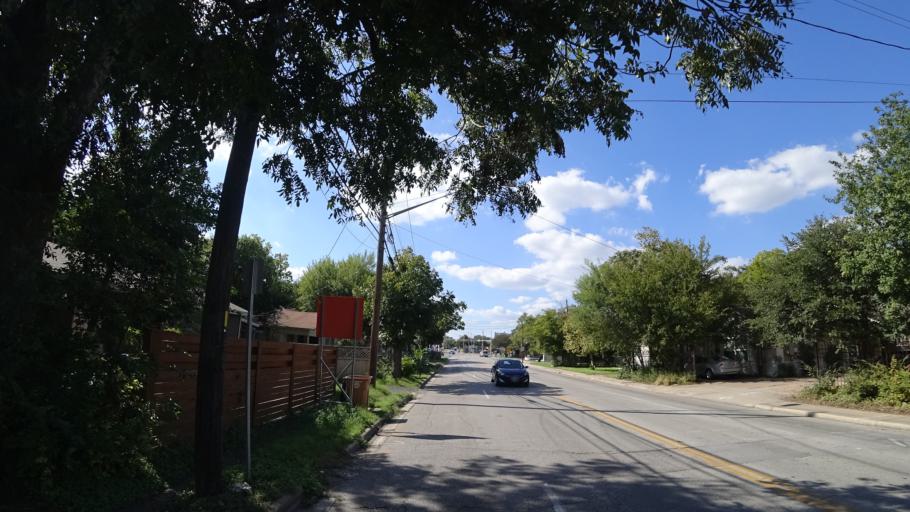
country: US
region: Texas
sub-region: Travis County
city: Austin
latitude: 30.3114
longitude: -97.7140
